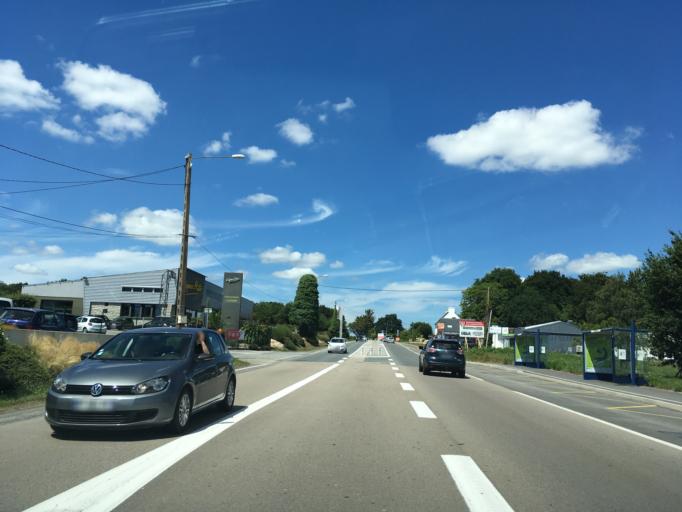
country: FR
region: Brittany
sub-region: Departement du Finistere
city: Quimper
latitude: 47.9652
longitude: -4.0839
